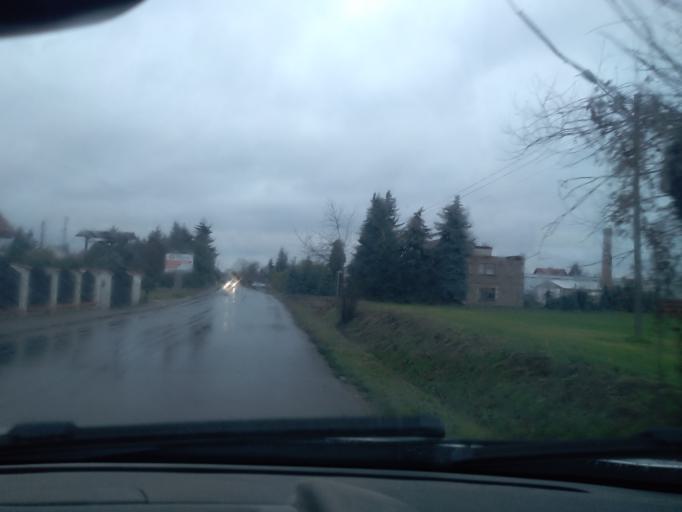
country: PL
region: Greater Poland Voivodeship
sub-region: Powiat obornicki
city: Oborniki
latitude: 52.6563
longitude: 16.8419
